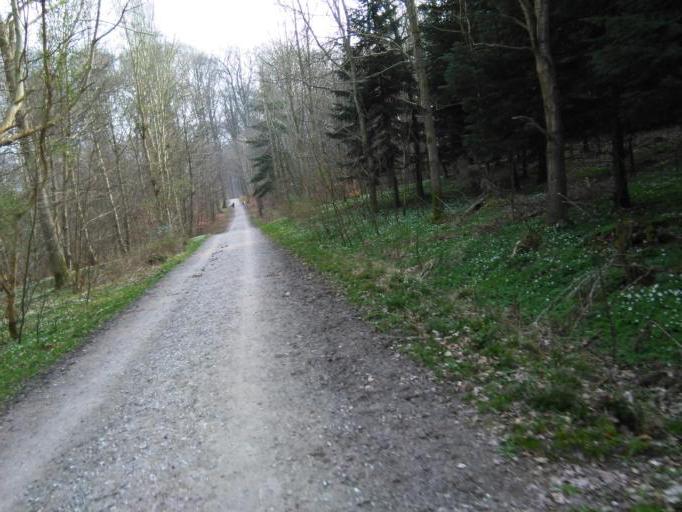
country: DK
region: Central Jutland
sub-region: Arhus Kommune
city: Beder
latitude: 56.0776
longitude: 10.2470
